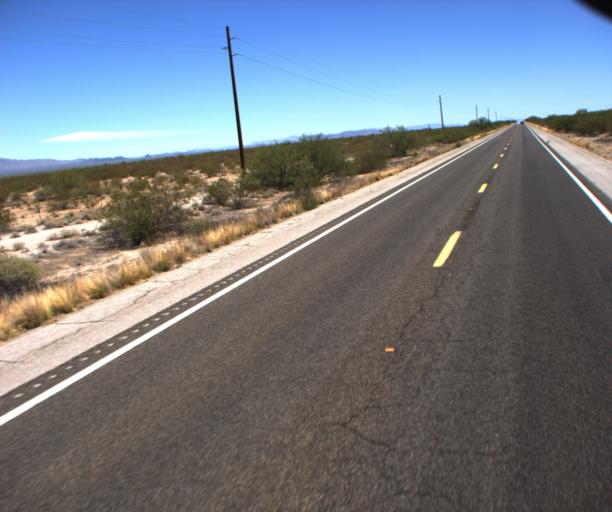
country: US
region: Arizona
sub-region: La Paz County
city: Salome
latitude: 33.8665
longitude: -113.4040
